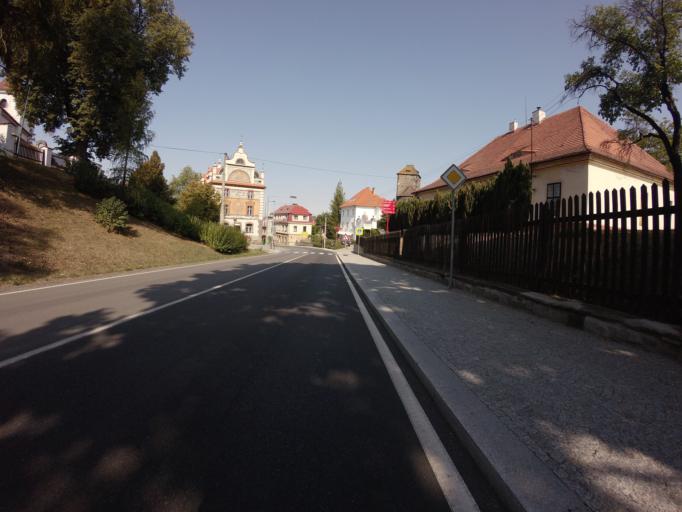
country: CZ
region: Central Bohemia
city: Tynec nad Sazavou
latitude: 49.8296
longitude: 14.5936
